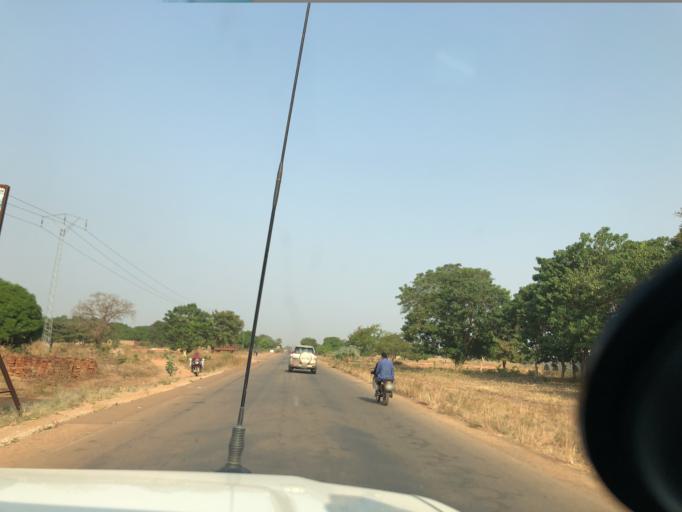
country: TD
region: Logone Occidental
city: Moundou
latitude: 8.5839
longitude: 16.0261
